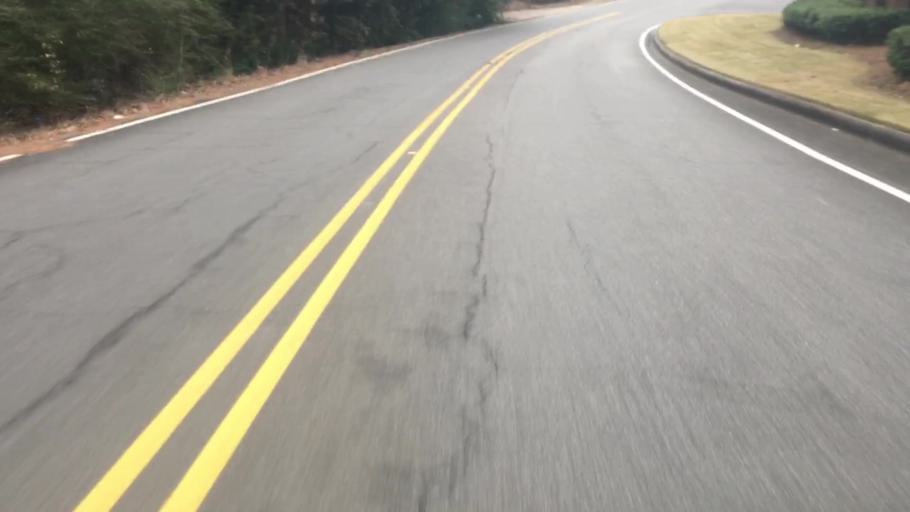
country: US
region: Alabama
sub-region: Jefferson County
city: Vestavia Hills
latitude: 33.4324
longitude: -86.7574
